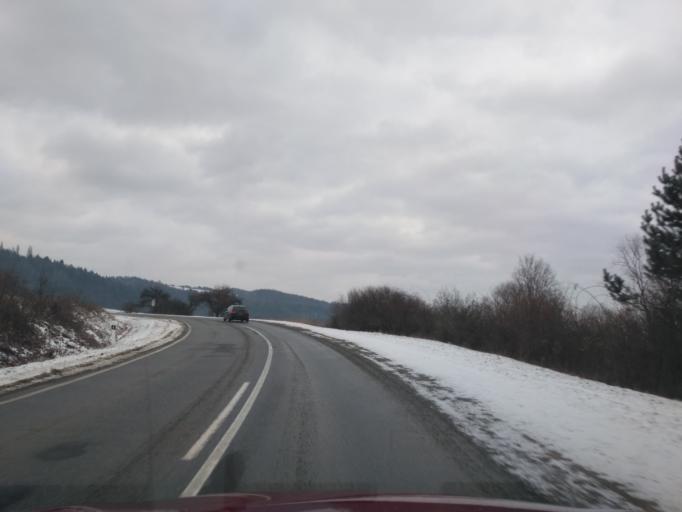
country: SK
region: Presovsky
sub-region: Okres Presov
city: Presov
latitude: 48.9537
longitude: 21.1585
